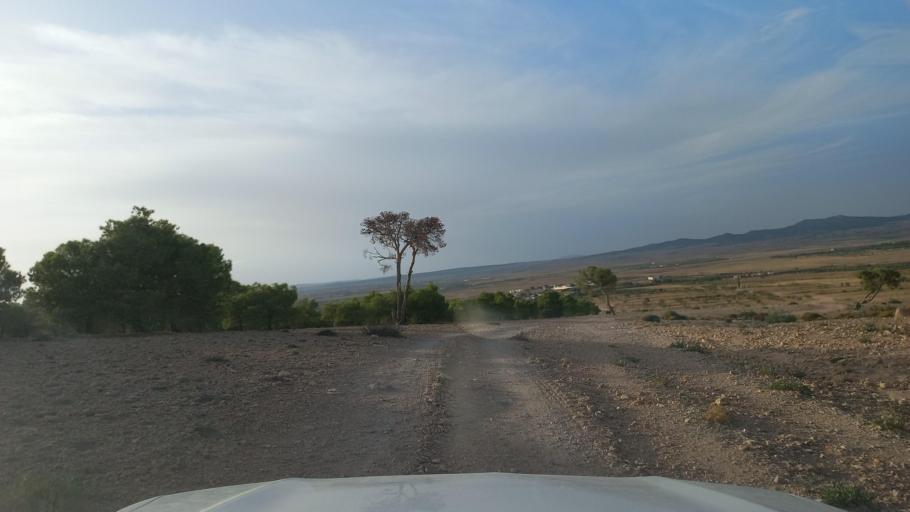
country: TN
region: Al Qasrayn
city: Sbiba
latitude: 35.4151
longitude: 8.8953
